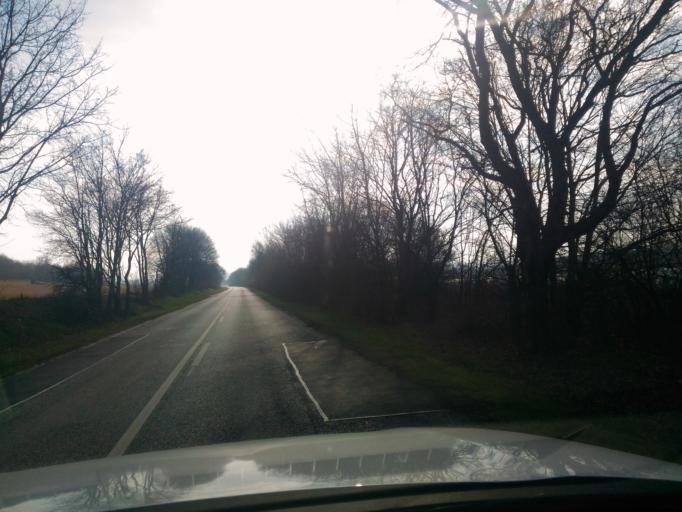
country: HU
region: Fejer
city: Etyek
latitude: 47.4840
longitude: 18.7709
